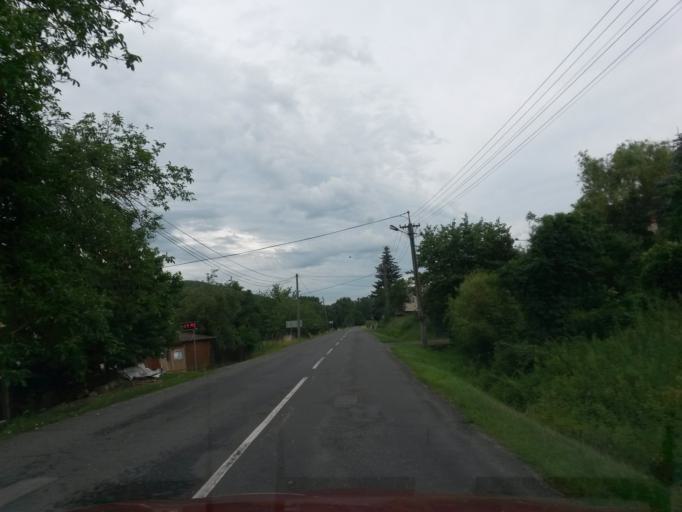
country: SK
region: Banskobystricky
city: Velky Krtis
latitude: 48.3537
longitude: 19.4070
